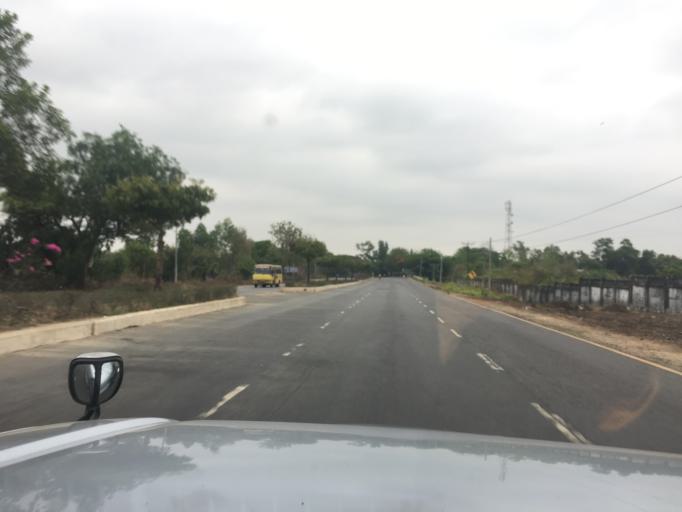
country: MM
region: Bago
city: Thanatpin
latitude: 17.2009
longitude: 96.4072
